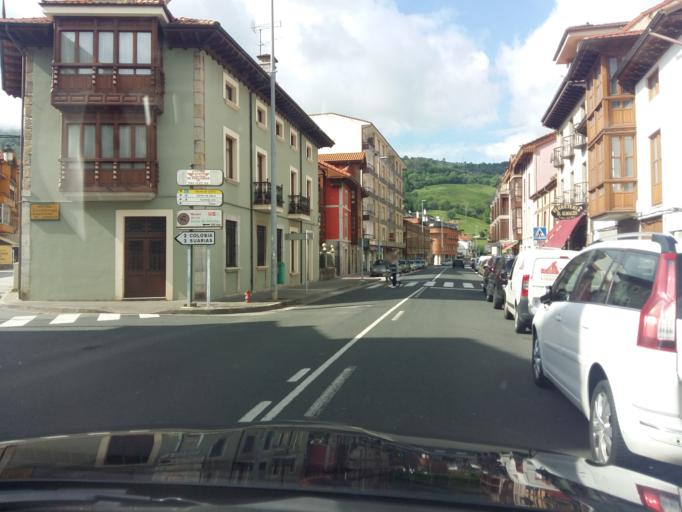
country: ES
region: Cantabria
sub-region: Provincia de Cantabria
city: Tresviso
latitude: 43.3240
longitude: -4.5838
